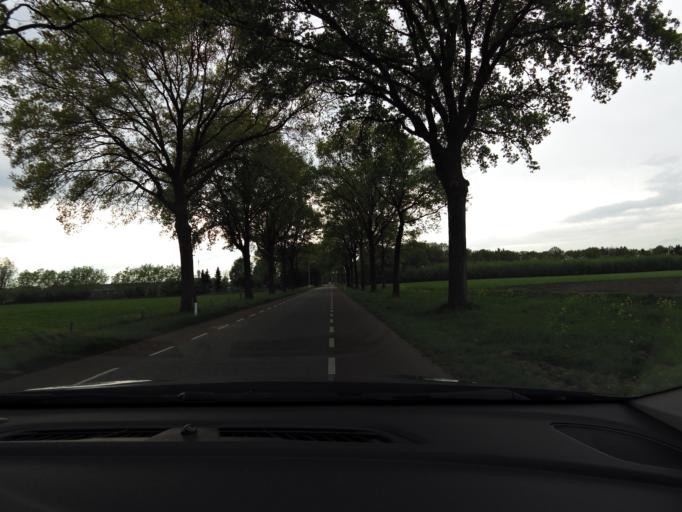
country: NL
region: North Brabant
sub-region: Gemeente Loon op Zand
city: Loon op Zand
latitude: 51.6108
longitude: 5.0994
